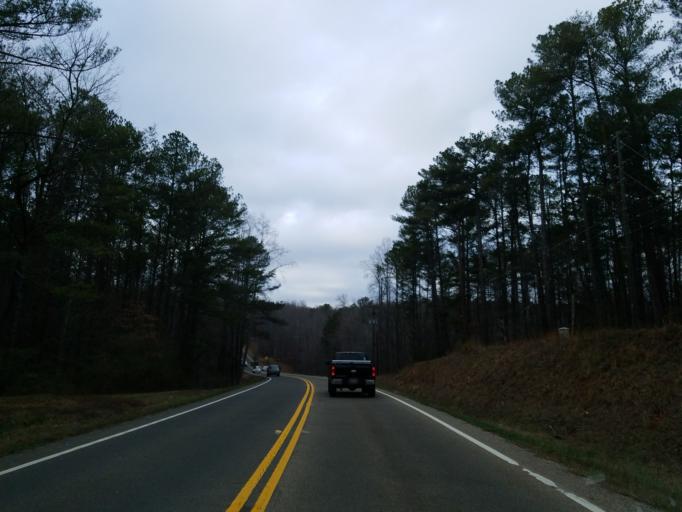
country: US
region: Georgia
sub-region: Cherokee County
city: Canton
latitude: 34.2826
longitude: -84.5112
